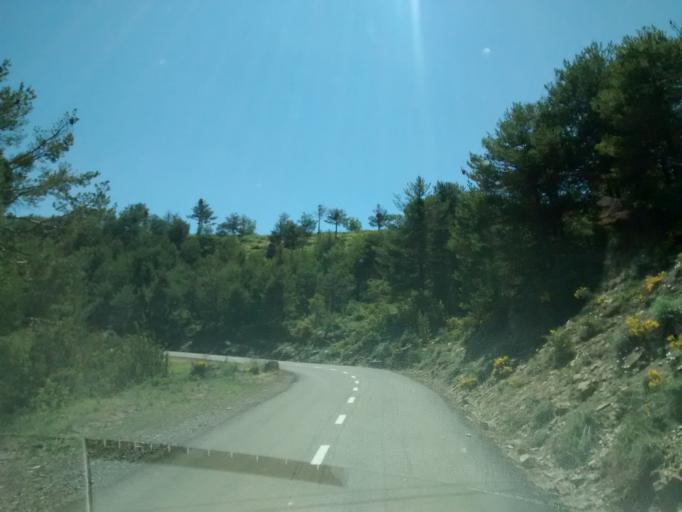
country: ES
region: Aragon
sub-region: Provincia de Huesca
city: Borau
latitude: 42.6670
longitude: -0.5985
